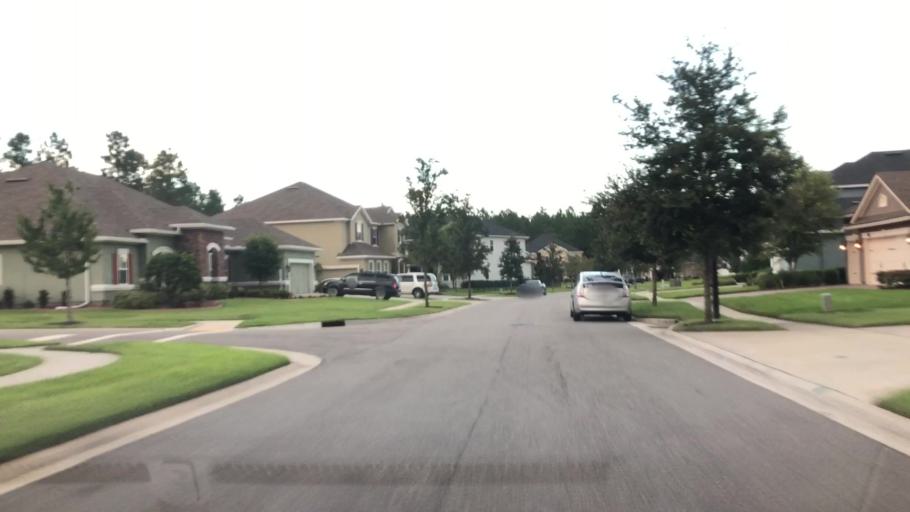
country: US
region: Florida
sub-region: Saint Johns County
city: Palm Valley
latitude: 30.0956
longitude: -81.4606
